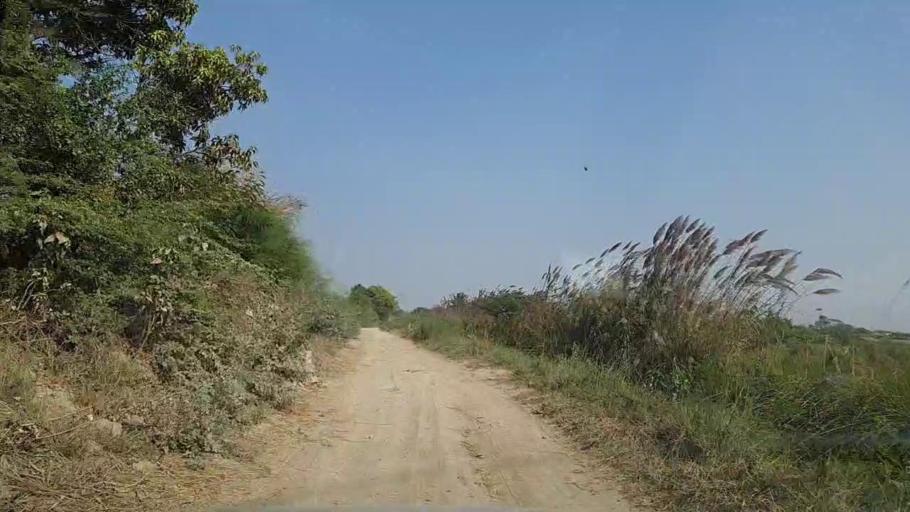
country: PK
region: Sindh
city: Mirpur Sakro
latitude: 24.5561
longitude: 67.5808
